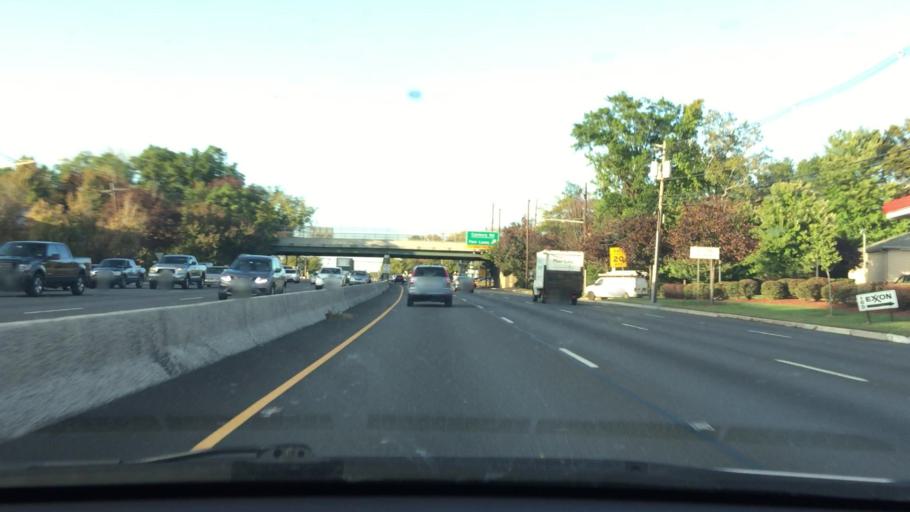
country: US
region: New Jersey
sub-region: Bergen County
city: Paramus
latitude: 40.9272
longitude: -74.0708
